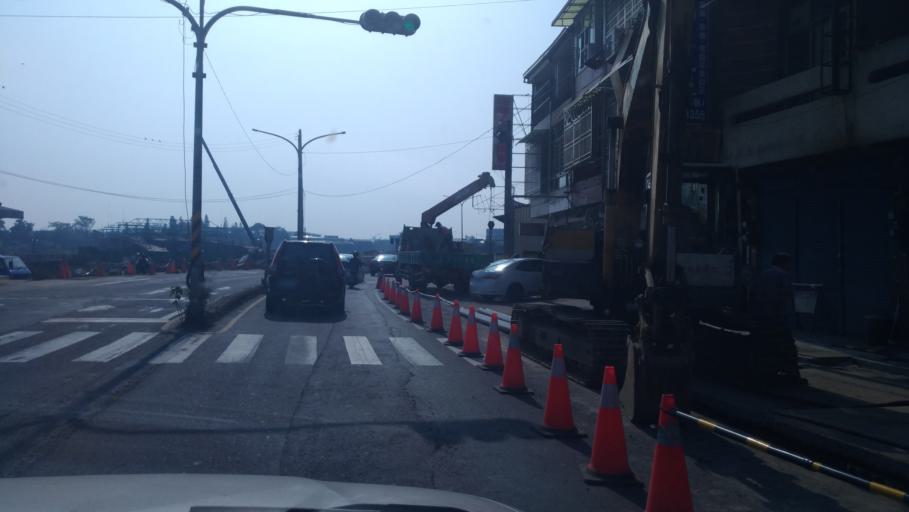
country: TW
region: Taiwan
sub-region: Chiayi
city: Jiayi Shi
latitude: 23.5120
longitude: 120.4325
